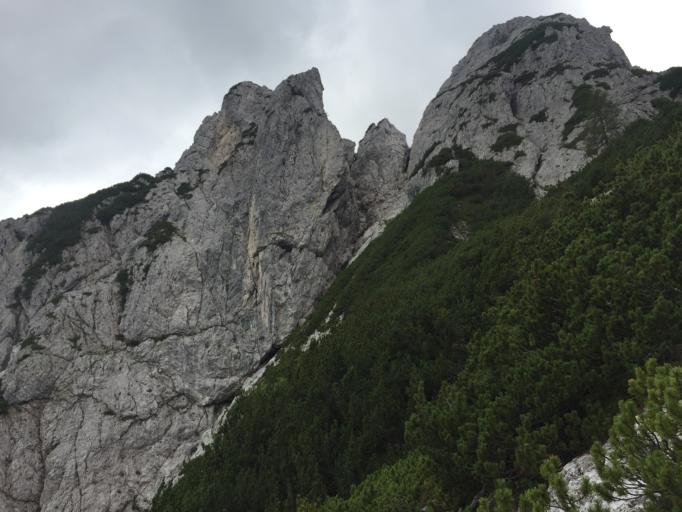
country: IT
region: Friuli Venezia Giulia
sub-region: Provincia di Udine
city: Tarvisio
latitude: 46.4602
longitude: 13.5906
